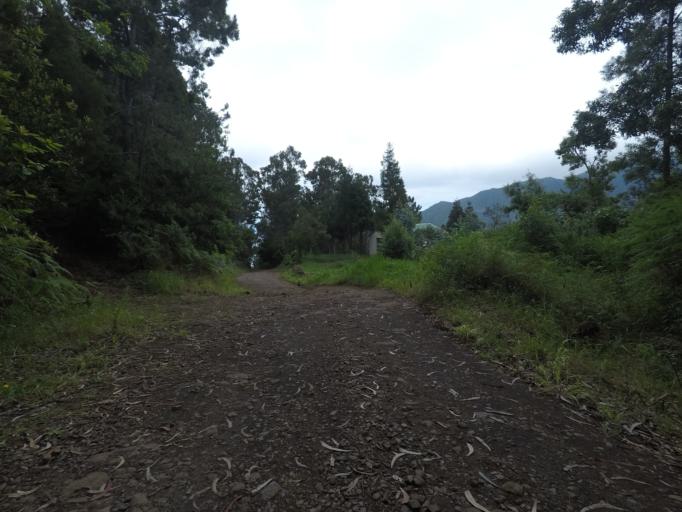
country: PT
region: Madeira
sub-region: Sao Vicente
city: Sao Vicente
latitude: 32.7768
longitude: -17.0480
